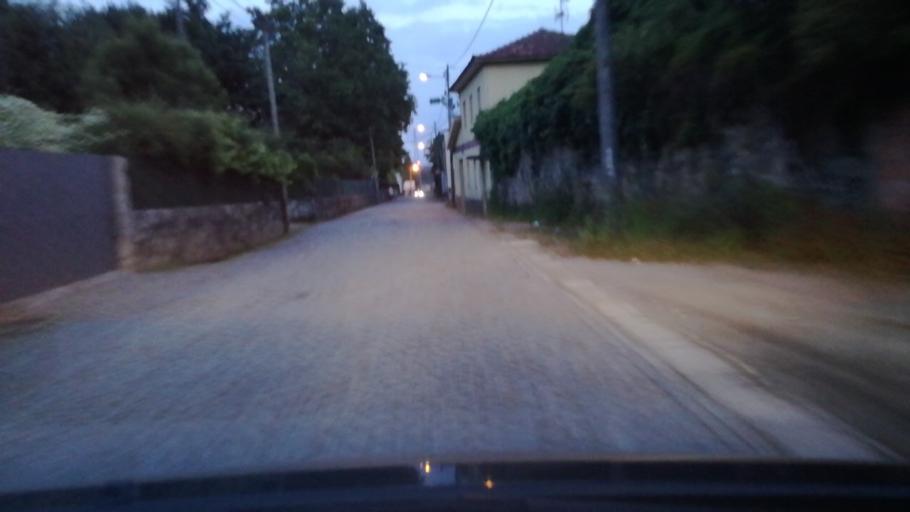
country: PT
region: Porto
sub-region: Maia
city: Anta
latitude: 41.2687
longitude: -8.6070
